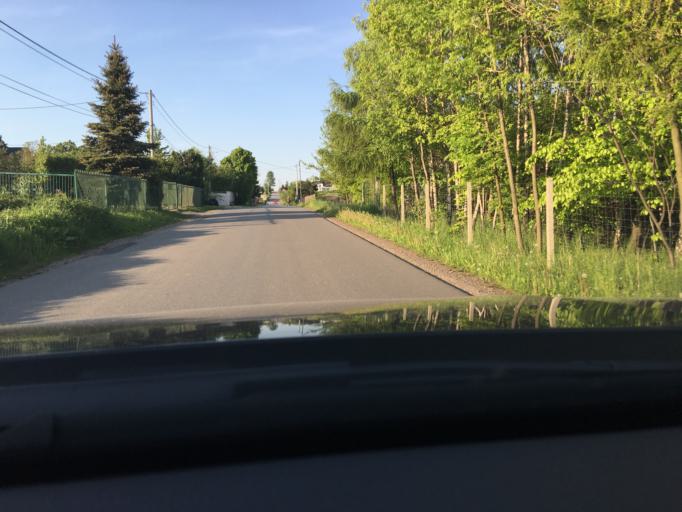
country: PL
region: Lesser Poland Voivodeship
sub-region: Powiat krakowski
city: Jerzmanowice
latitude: 50.2171
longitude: 19.7442
